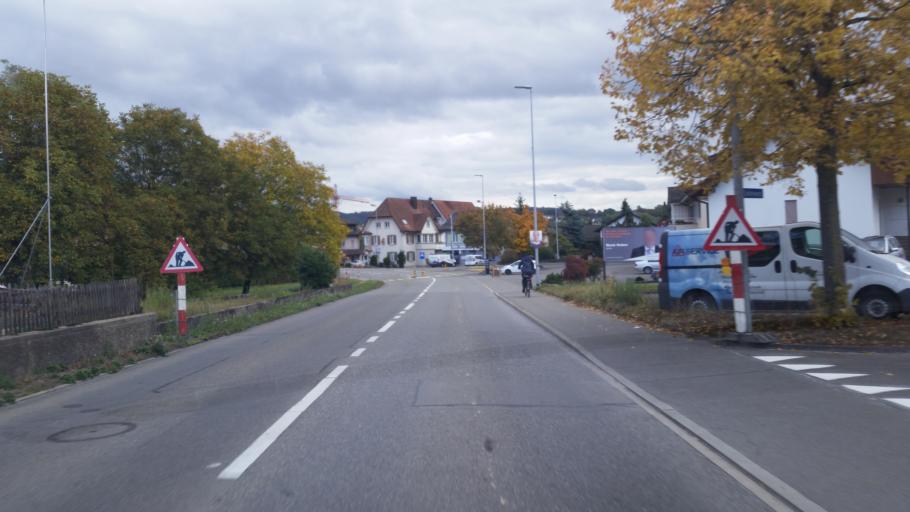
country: CH
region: Aargau
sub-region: Bezirk Zurzach
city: Klingnau
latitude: 47.5713
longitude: 8.2451
